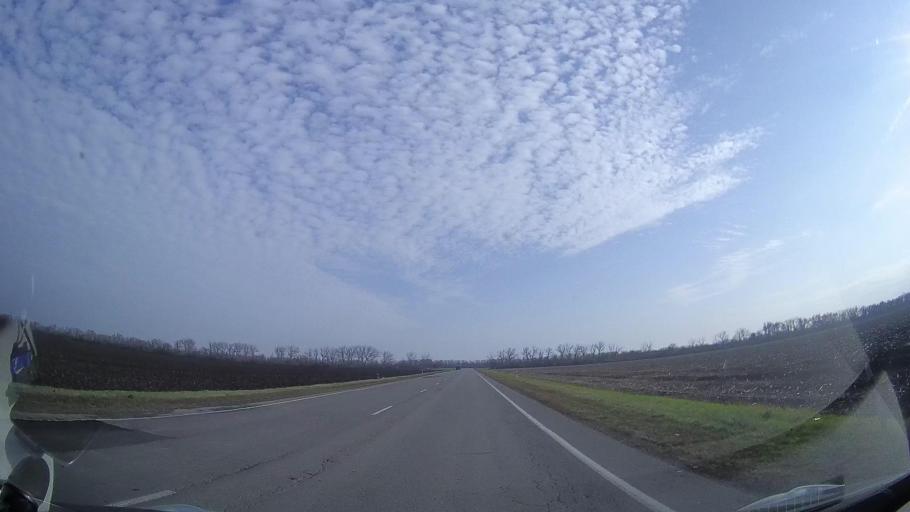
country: RU
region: Rostov
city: Tselina
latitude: 46.5218
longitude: 41.1434
